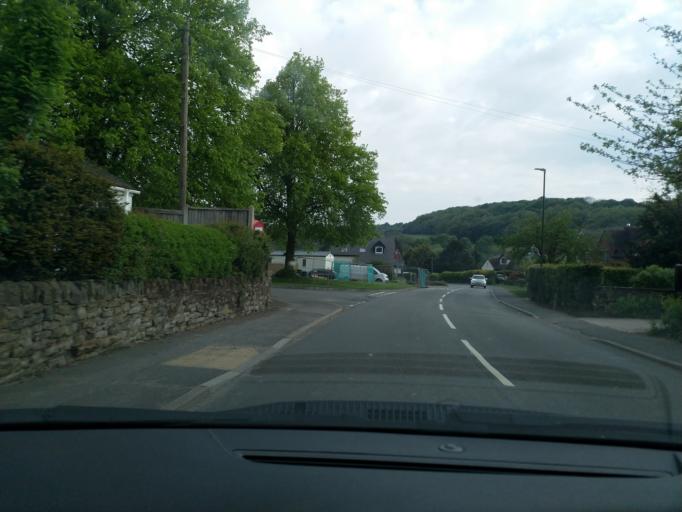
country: GB
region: England
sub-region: Derbyshire
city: Dronfield
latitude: 53.2751
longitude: -1.4963
